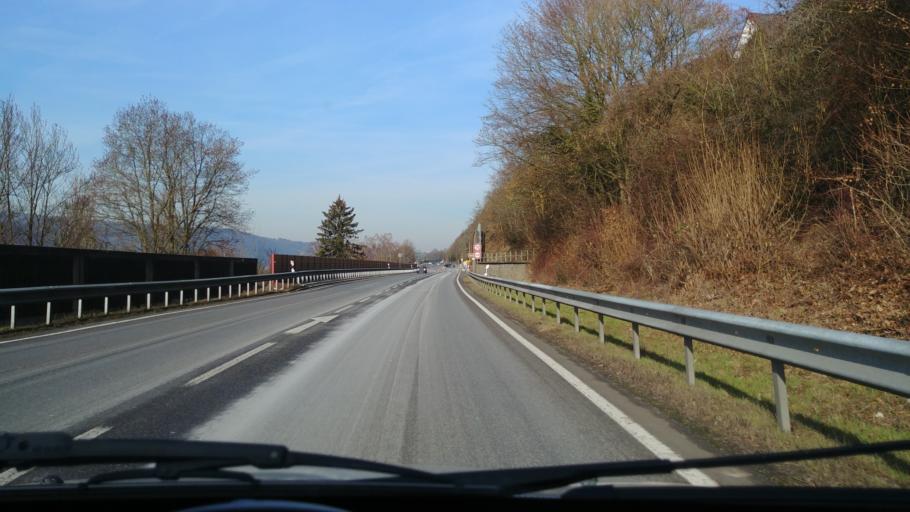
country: DE
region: Rheinland-Pfalz
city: Lahnstein
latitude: 50.2998
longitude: 7.6148
